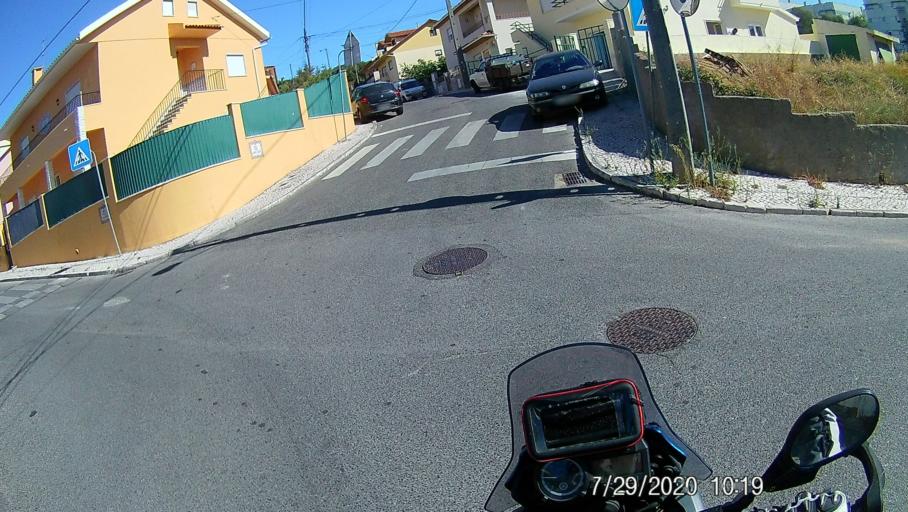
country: PT
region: Lisbon
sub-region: Cascais
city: Estoril
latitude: 38.7242
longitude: -9.3756
